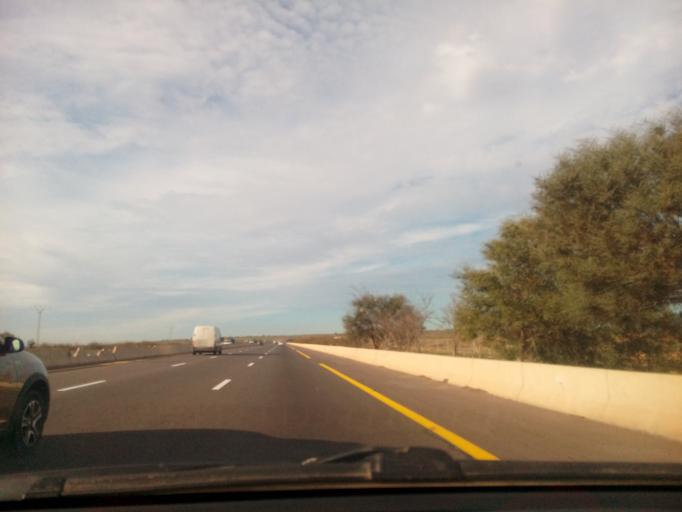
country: DZ
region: Mascara
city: Sig
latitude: 35.5722
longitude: -0.2931
